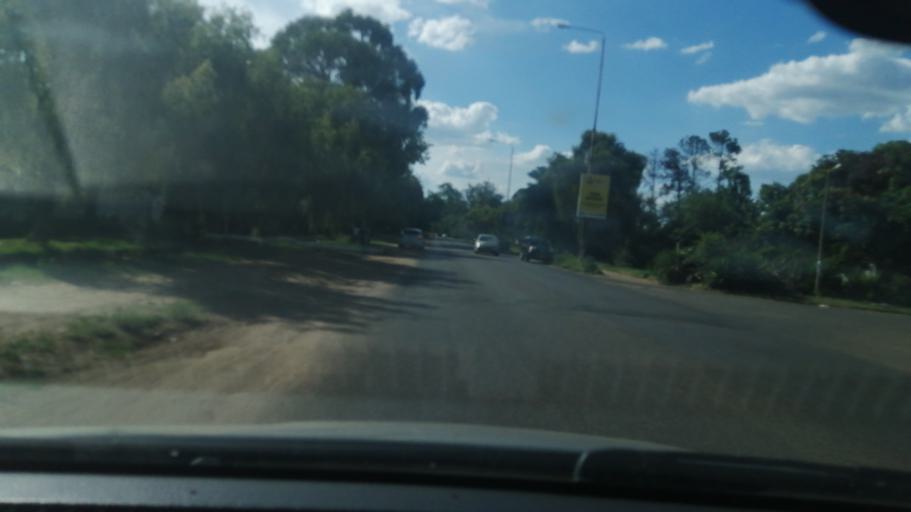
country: ZW
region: Harare
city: Harare
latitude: -17.7751
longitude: 31.0636
